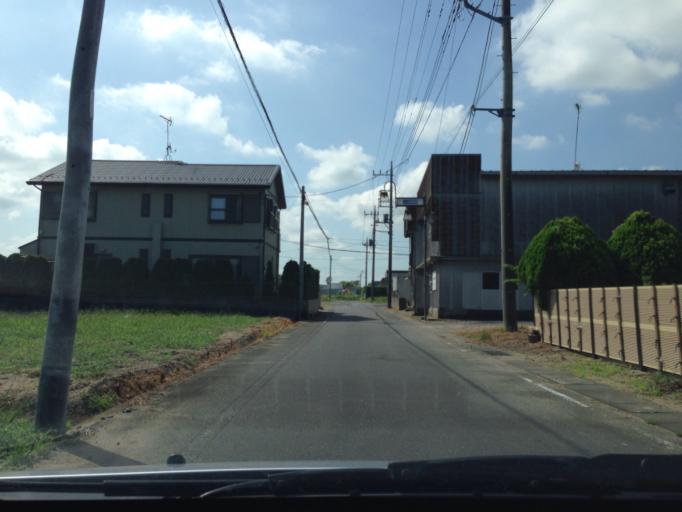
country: JP
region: Ibaraki
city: Inashiki
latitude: 36.0042
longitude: 140.3699
